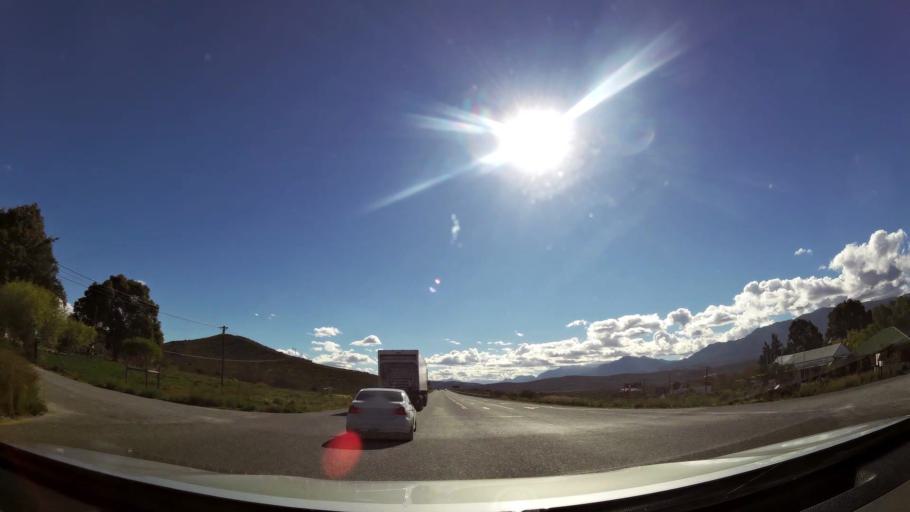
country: ZA
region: Western Cape
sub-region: Cape Winelands District Municipality
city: Worcester
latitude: -33.7619
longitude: 19.7395
